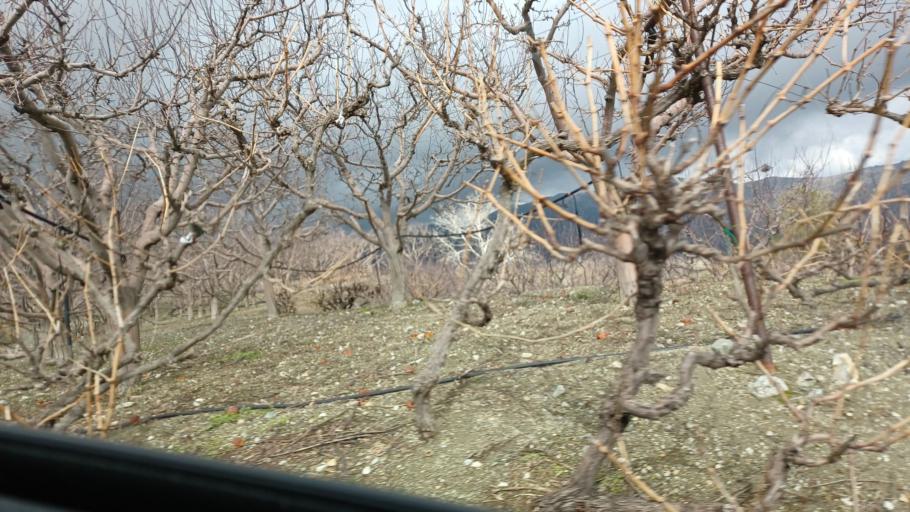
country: CY
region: Limassol
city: Kyperounta
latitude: 34.9249
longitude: 32.9666
